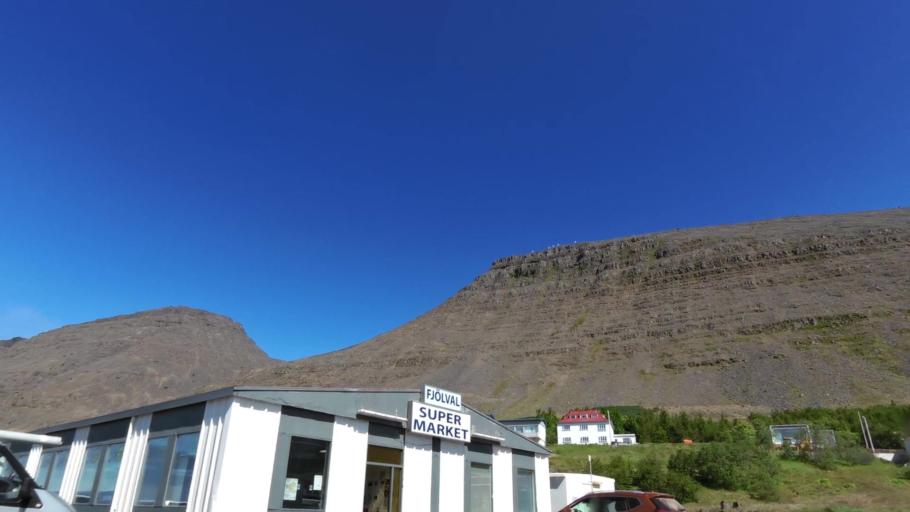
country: IS
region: West
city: Olafsvik
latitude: 65.5982
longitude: -24.0010
